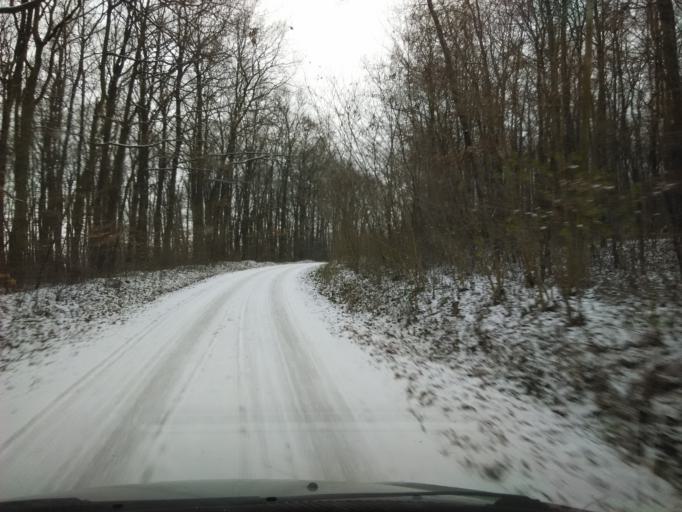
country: SK
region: Nitriansky
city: Zlate Moravce
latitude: 48.4422
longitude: 18.3534
